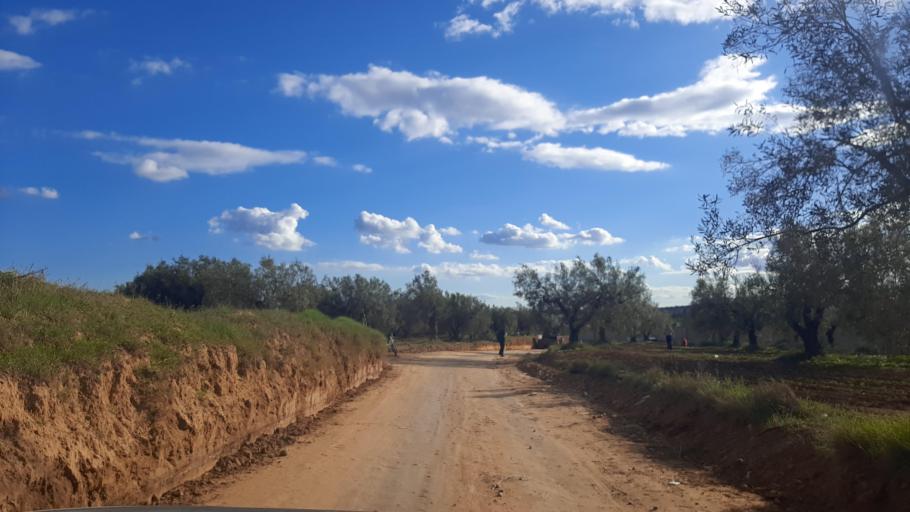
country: TN
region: Nabul
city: Al Hammamat
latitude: 36.4249
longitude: 10.5079
